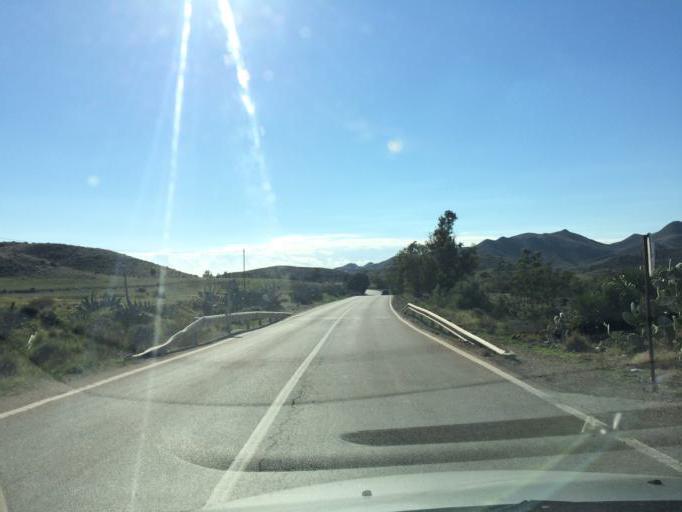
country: ES
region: Andalusia
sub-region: Provincia de Almeria
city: San Jose
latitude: 36.7876
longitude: -2.1091
